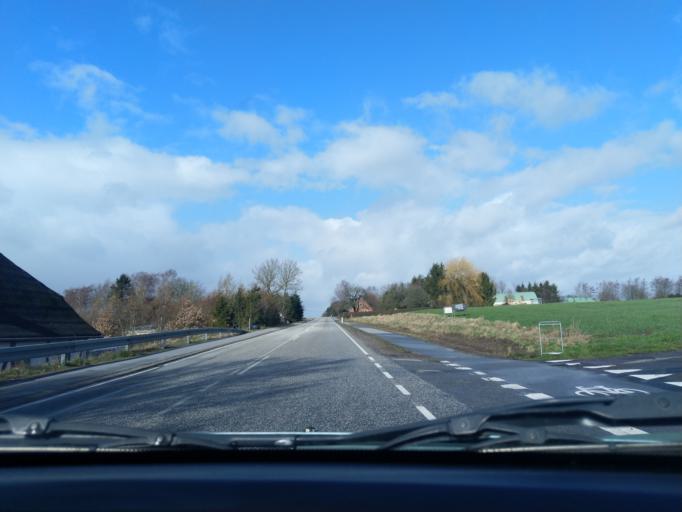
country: DK
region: Zealand
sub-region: Naestved Kommune
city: Naestved
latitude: 55.3063
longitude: 11.6882
